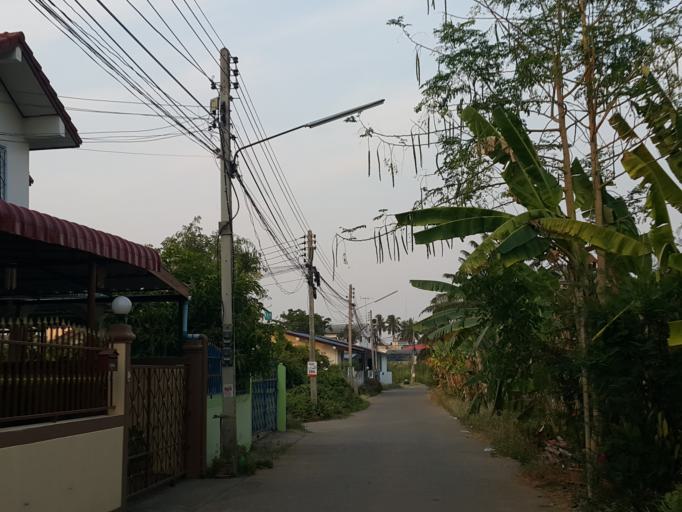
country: TH
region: Sukhothai
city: Sawankhalok
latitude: 17.2978
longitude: 99.8335
